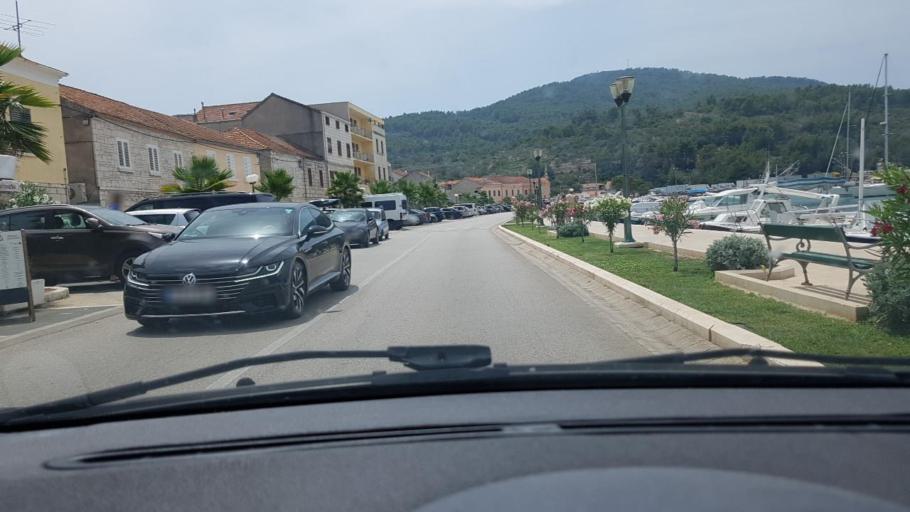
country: HR
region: Dubrovacko-Neretvanska
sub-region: Grad Dubrovnik
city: Vela Luka
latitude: 42.9602
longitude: 16.7134
